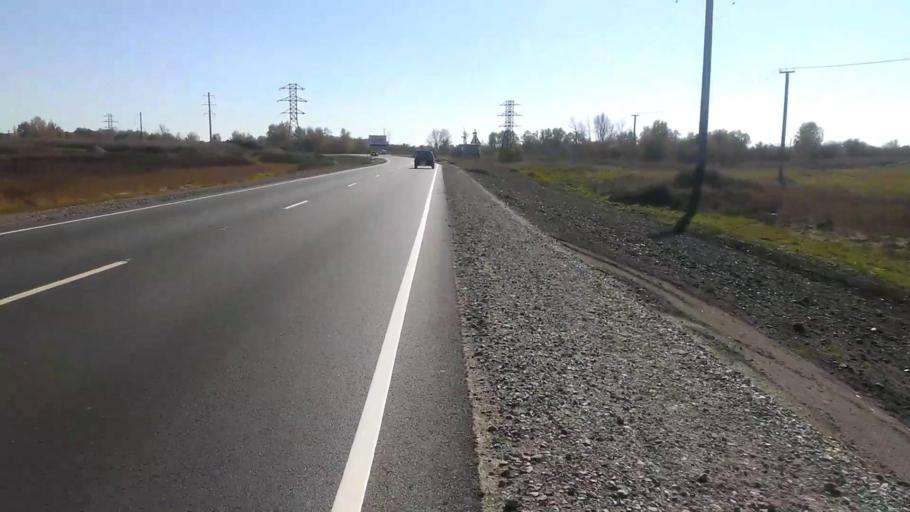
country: RU
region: Altai Krai
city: Sannikovo
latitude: 53.3313
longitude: 83.9383
